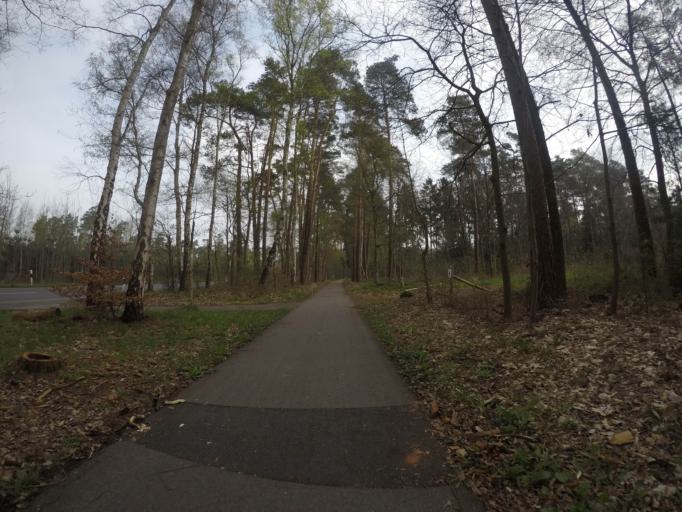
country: DE
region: North Rhine-Westphalia
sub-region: Regierungsbezirk Munster
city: Isselburg
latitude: 51.8383
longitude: 6.4975
